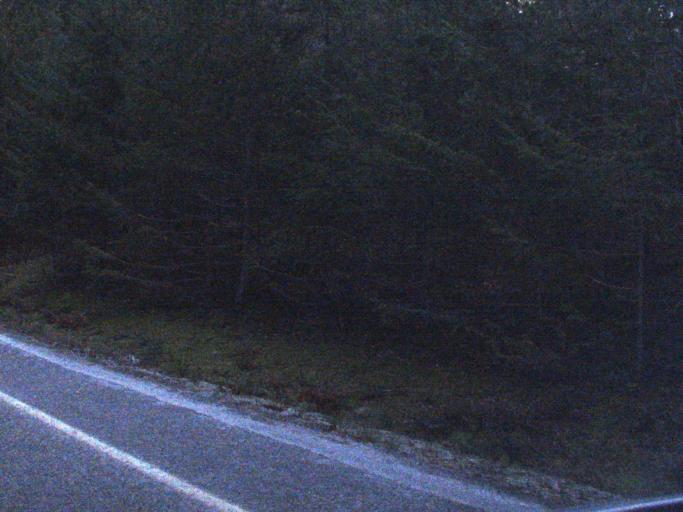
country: US
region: Washington
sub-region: Snohomish County
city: Darrington
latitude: 48.7102
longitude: -121.1278
